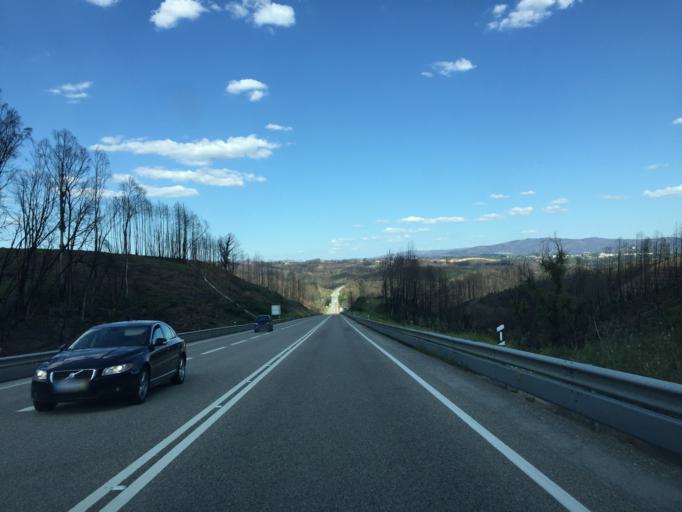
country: PT
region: Leiria
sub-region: Pedrogao Grande
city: Pedrogao Grande
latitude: 39.9247
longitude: -8.2055
